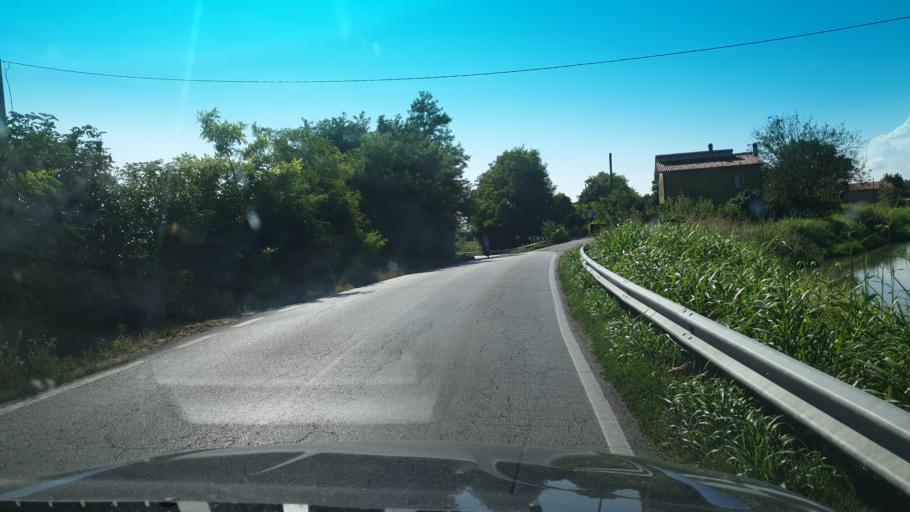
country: IT
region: Veneto
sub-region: Provincia di Rovigo
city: Grignano Polesine
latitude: 45.0693
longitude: 11.7269
